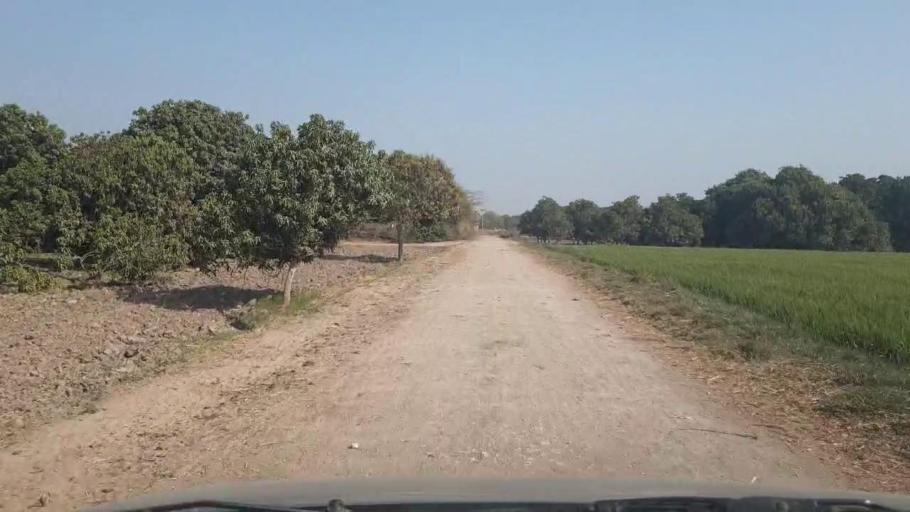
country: PK
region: Sindh
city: Mirwah Gorchani
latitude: 25.2573
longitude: 69.0916
